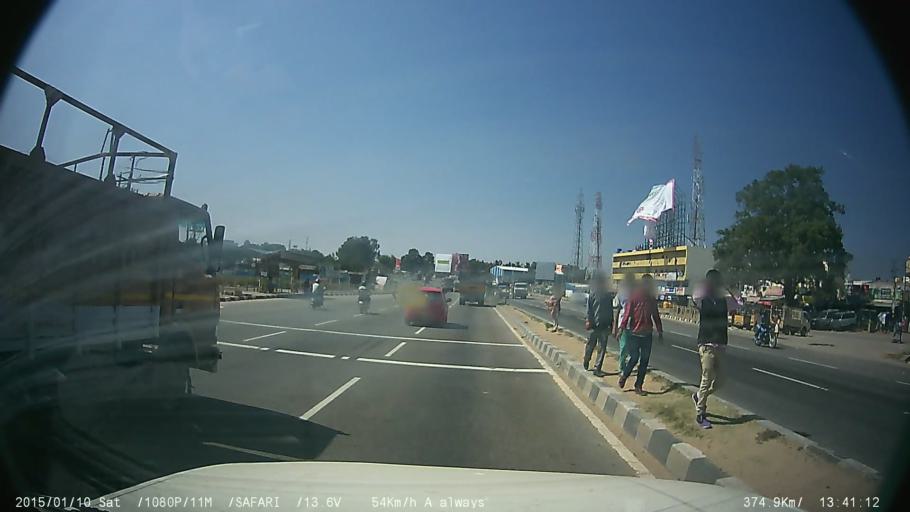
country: IN
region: Karnataka
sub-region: Bangalore Urban
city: Anekal
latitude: 12.7851
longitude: 77.7517
